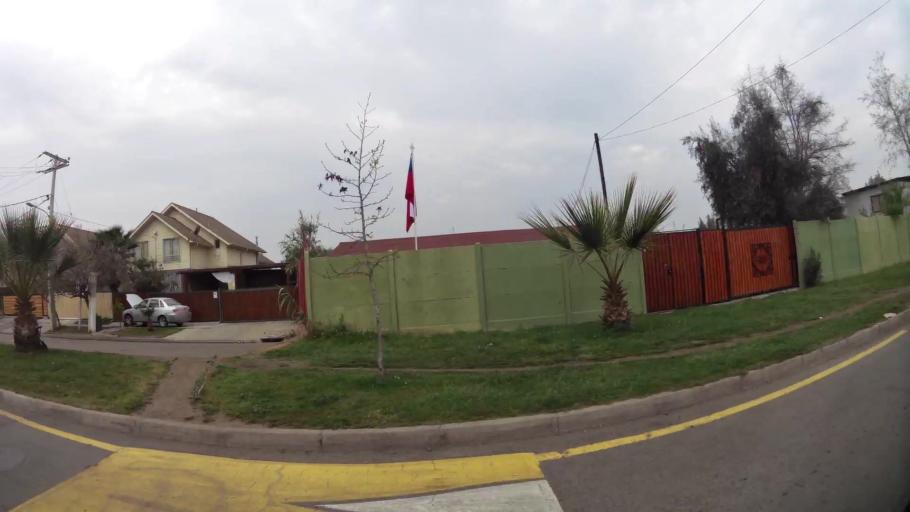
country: CL
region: Santiago Metropolitan
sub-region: Provincia de Chacabuco
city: Chicureo Abajo
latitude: -33.2029
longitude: -70.6821
